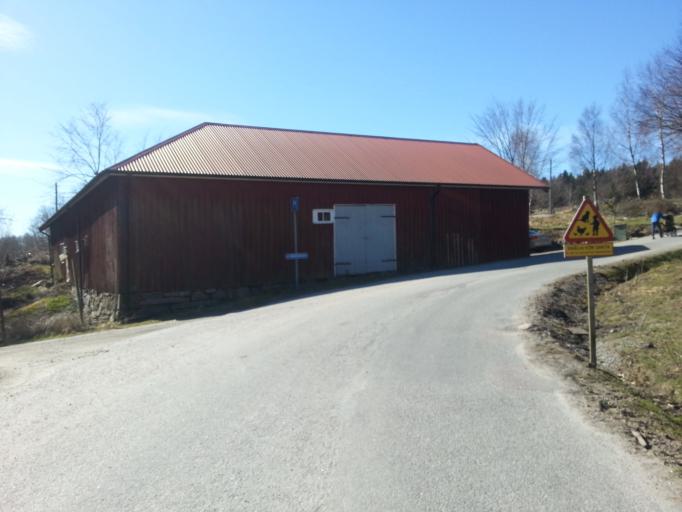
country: SE
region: Vaestra Goetaland
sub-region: Kungalvs Kommun
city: Kungalv
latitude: 57.9032
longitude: 11.9502
